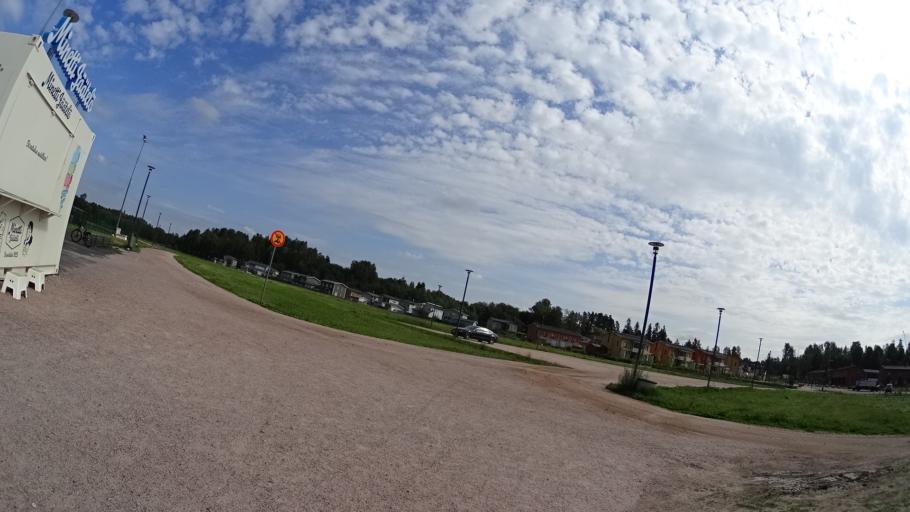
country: FI
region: Uusimaa
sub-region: Helsinki
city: Espoo
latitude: 60.1913
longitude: 24.5858
